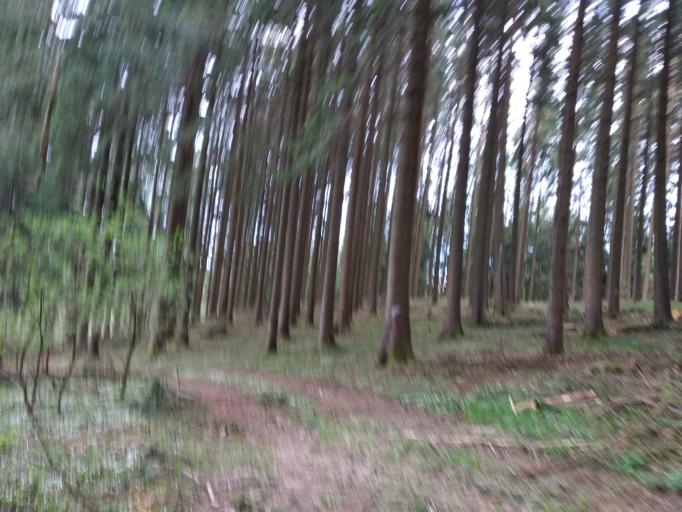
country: DE
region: Bavaria
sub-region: Swabia
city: Kronburg
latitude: 47.8914
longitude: 10.1756
